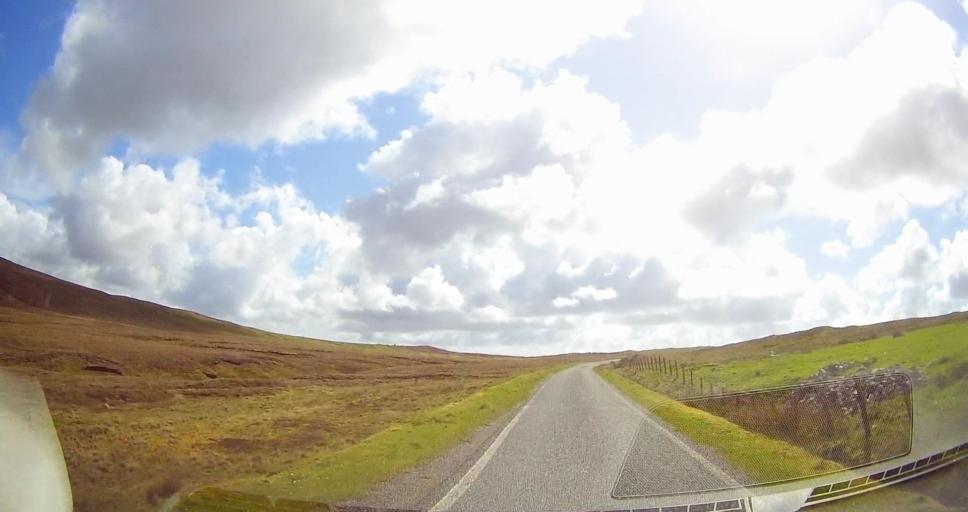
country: GB
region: Scotland
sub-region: Shetland Islands
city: Lerwick
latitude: 60.5058
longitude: -1.3899
